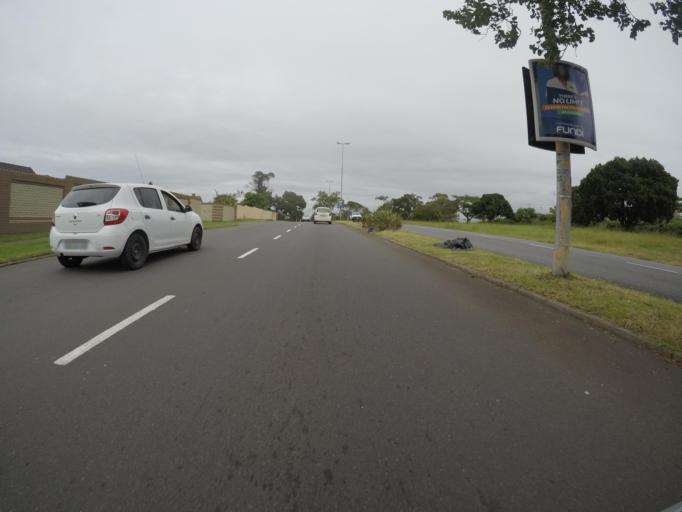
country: ZA
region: Eastern Cape
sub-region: Buffalo City Metropolitan Municipality
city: East London
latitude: -32.9873
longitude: 27.8945
